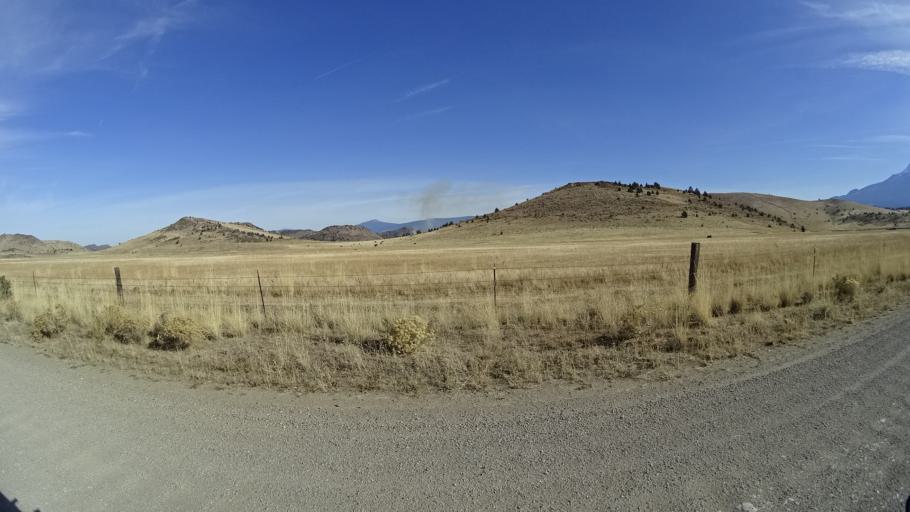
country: US
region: California
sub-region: Siskiyou County
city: Weed
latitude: 41.5060
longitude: -122.4587
